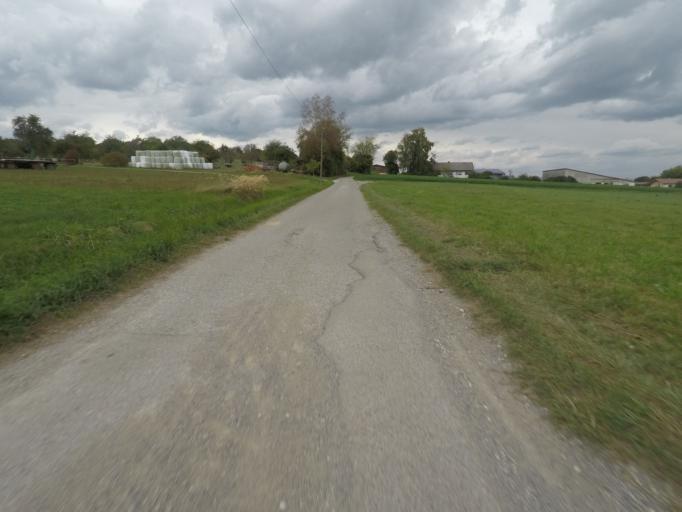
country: DE
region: Baden-Wuerttemberg
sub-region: Regierungsbezirk Stuttgart
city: Filderstadt
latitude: 48.6611
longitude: 9.1927
